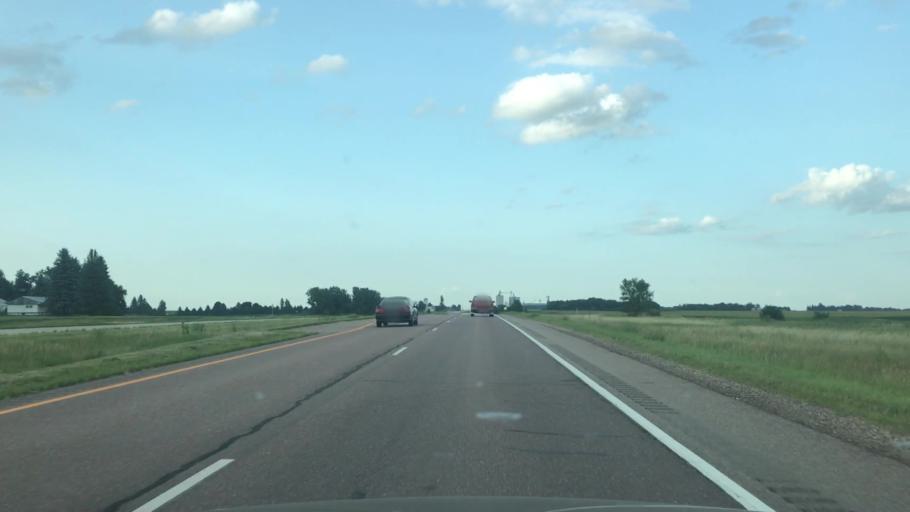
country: US
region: Minnesota
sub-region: Nobles County
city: Worthington
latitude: 43.6819
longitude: -95.4971
